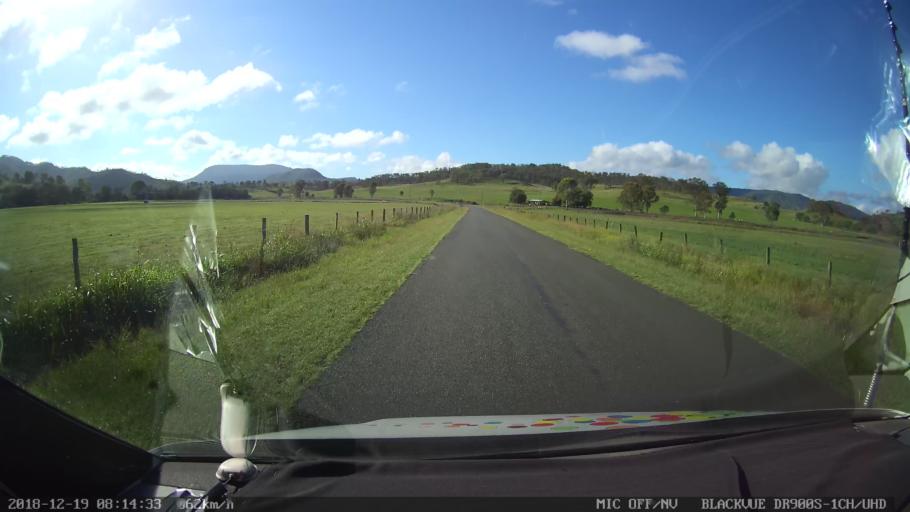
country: AU
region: Queensland
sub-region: Logan
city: Cedar Vale
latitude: -28.2484
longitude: 152.8915
